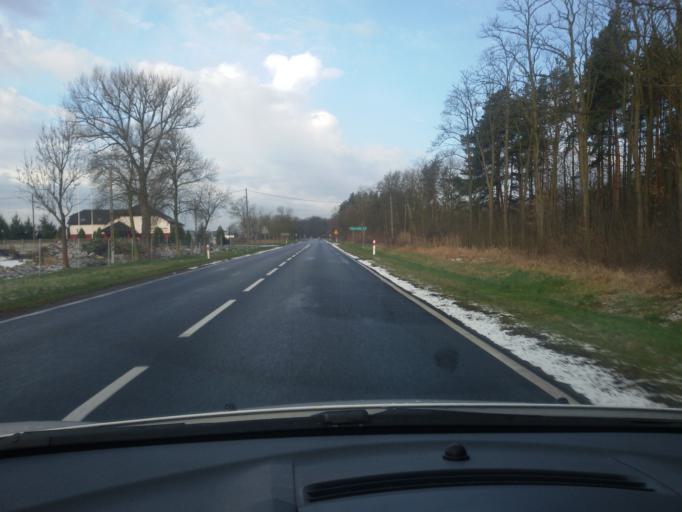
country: PL
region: Lower Silesian Voivodeship
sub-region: Powiat glogowski
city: Glogow
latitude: 51.6871
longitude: 16.1363
